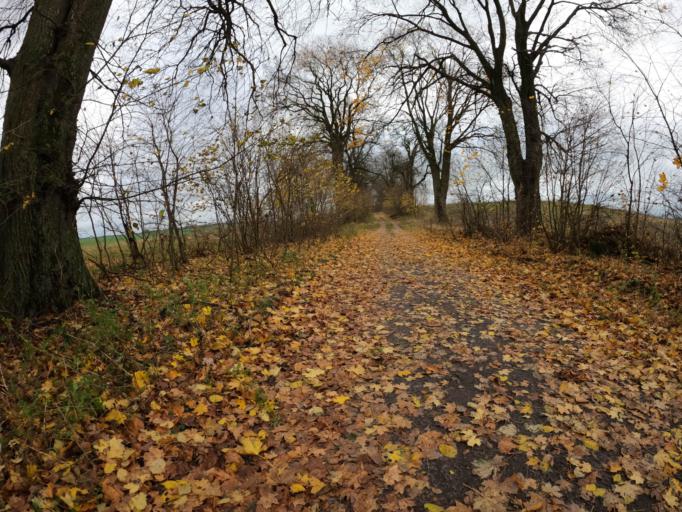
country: PL
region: West Pomeranian Voivodeship
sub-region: Powiat walecki
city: Tuczno
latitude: 53.2605
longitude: 16.1926
